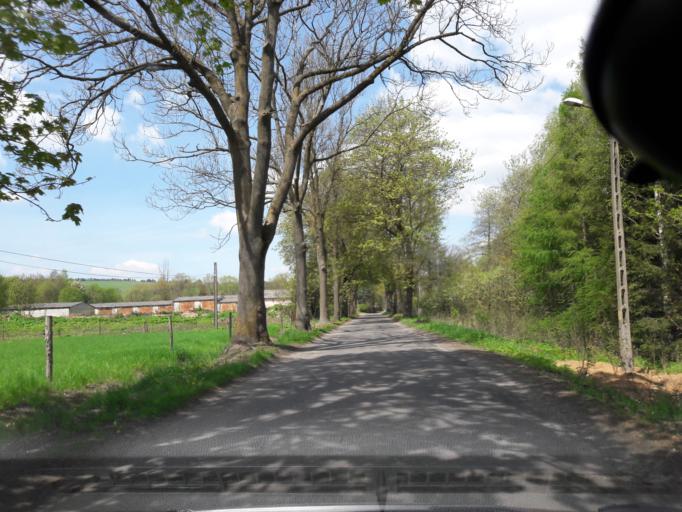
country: PL
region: Lower Silesian Voivodeship
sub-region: Powiat klodzki
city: Duszniki-Zdroj
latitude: 50.4260
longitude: 16.3720
